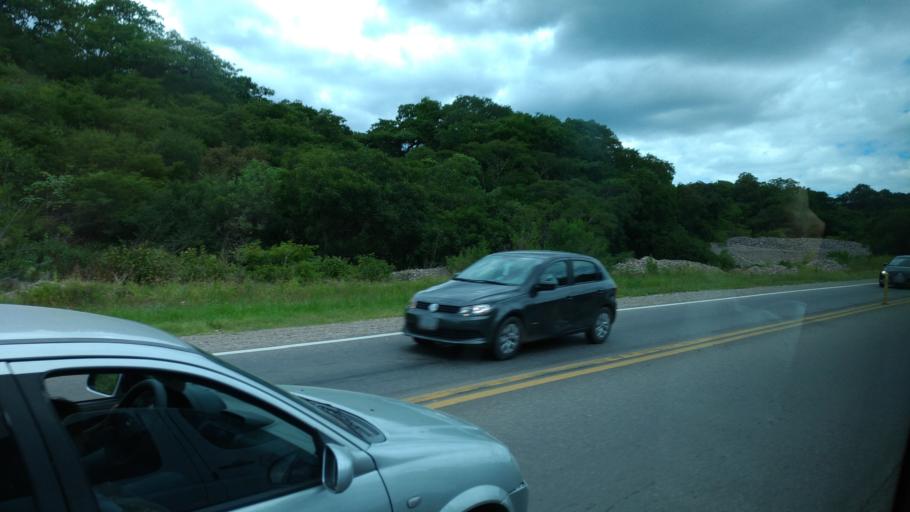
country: AR
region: Jujuy
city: La Mendieta
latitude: -24.3568
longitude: -64.9618
